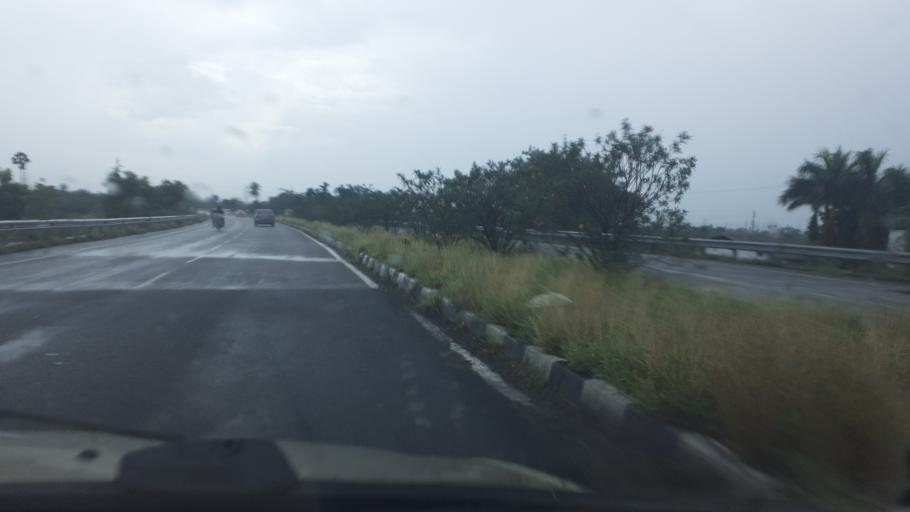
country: IN
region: Tamil Nadu
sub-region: Thoothukkudi
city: Kayattar
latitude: 8.9555
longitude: 77.7686
